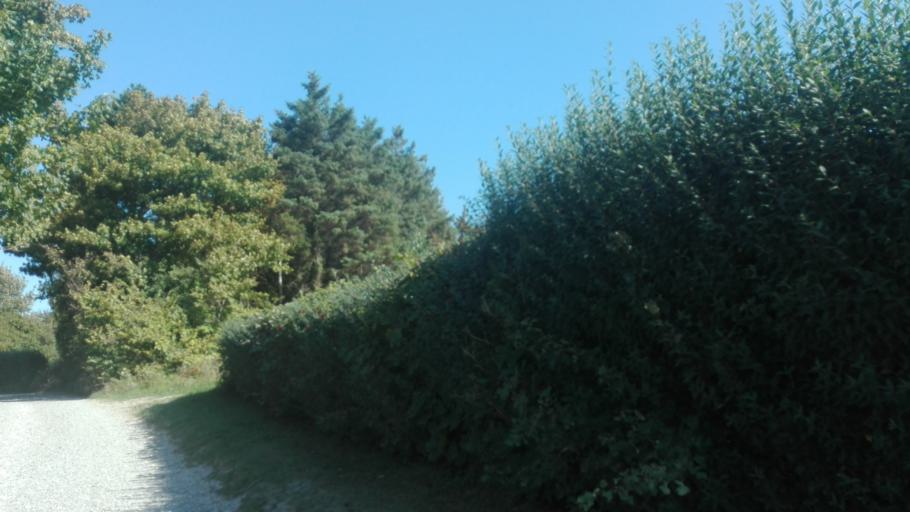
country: DK
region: Central Jutland
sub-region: Syddjurs Kommune
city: Ebeltoft
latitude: 56.2384
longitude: 10.7489
